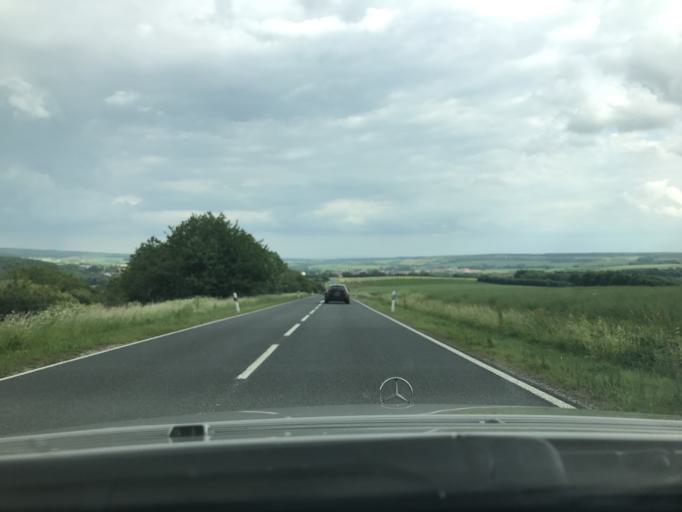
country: DE
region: Thuringia
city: Kefferhausen
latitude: 51.3302
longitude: 10.2896
